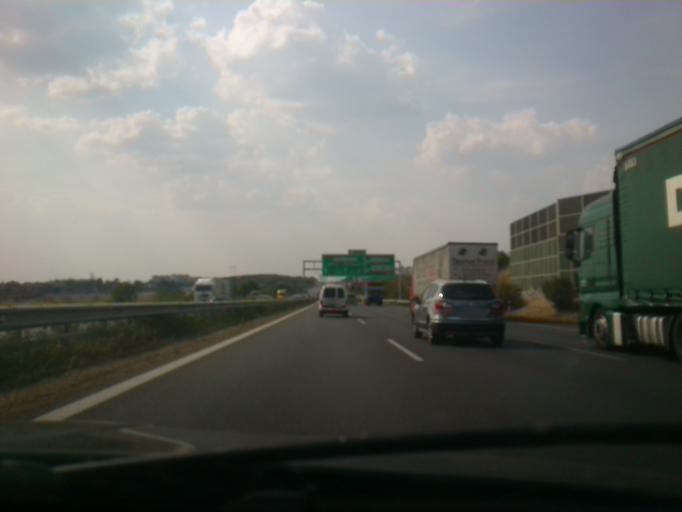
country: CZ
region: Central Bohemia
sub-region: Okres Praha-Zapad
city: Pruhonice
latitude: 50.0164
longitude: 14.5242
